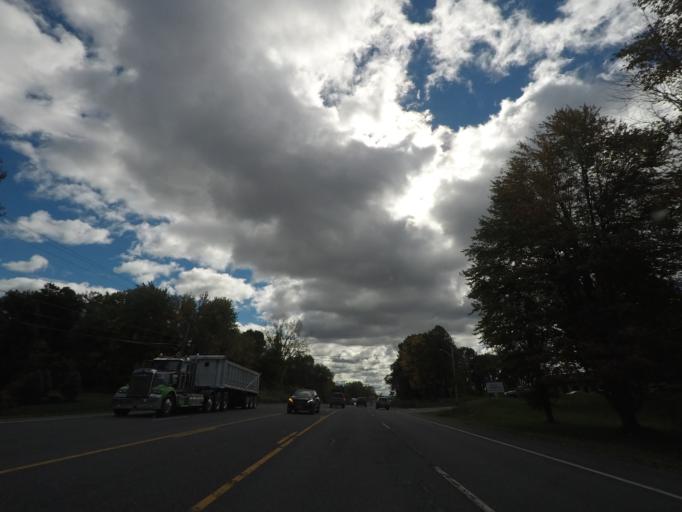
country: US
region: New York
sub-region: Saratoga County
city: Waterford
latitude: 42.8325
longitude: -73.7377
